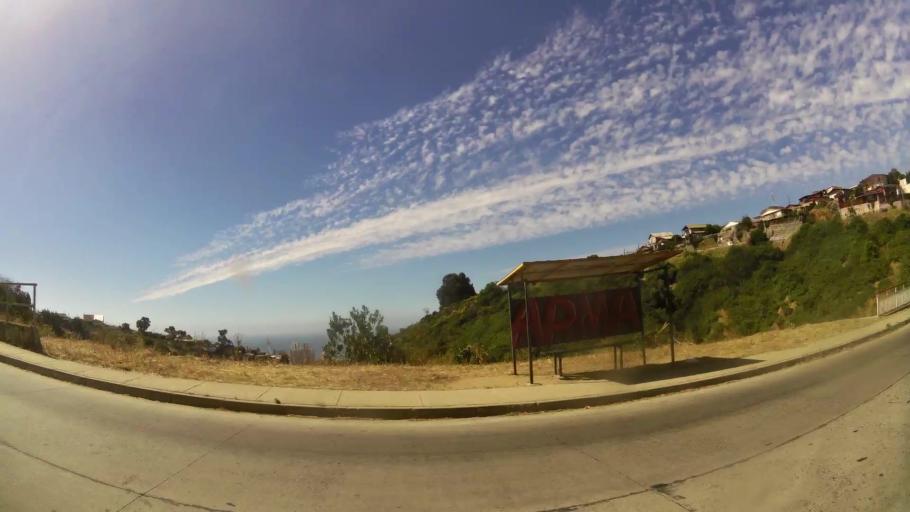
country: CL
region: Valparaiso
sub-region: Provincia de Valparaiso
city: Vina del Mar
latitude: -33.0436
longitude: -71.5743
